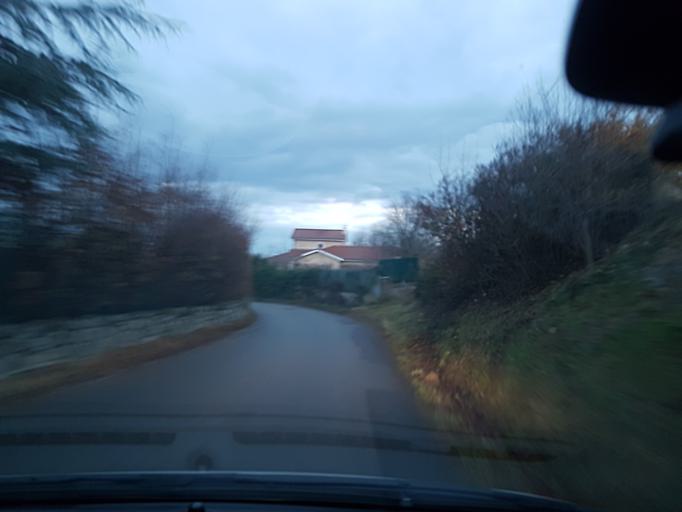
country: FR
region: Rhone-Alpes
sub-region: Departement du Rhone
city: Mornant
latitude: 45.6201
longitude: 4.6819
